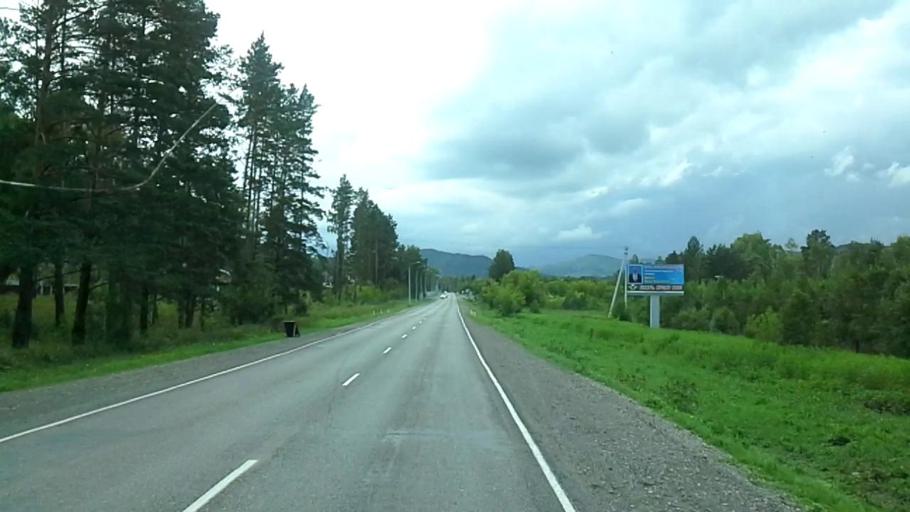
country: RU
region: Altay
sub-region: Mayminskiy Rayon
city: Manzherok
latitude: 51.8715
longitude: 85.7897
